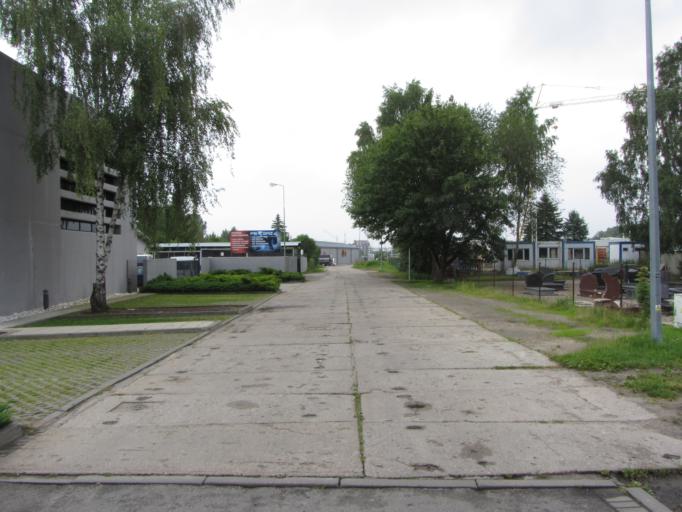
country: PL
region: West Pomeranian Voivodeship
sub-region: Powiat kolobrzeski
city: Kolobrzeg
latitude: 54.1583
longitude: 15.5629
